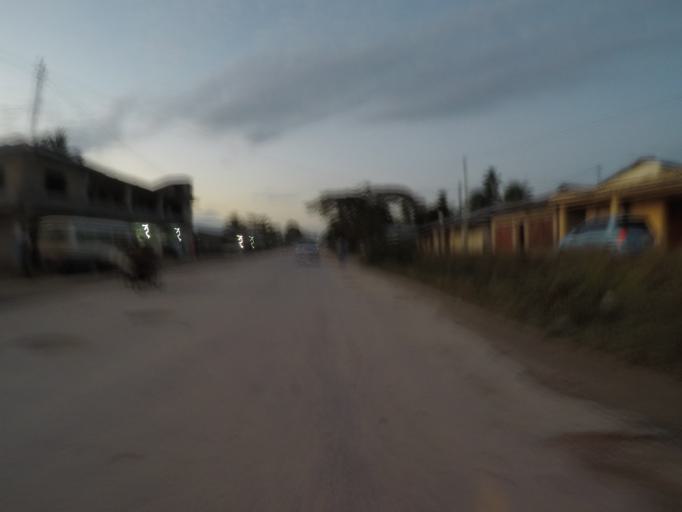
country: TZ
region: Zanzibar Central/South
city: Koani
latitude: -6.0858
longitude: 39.2227
